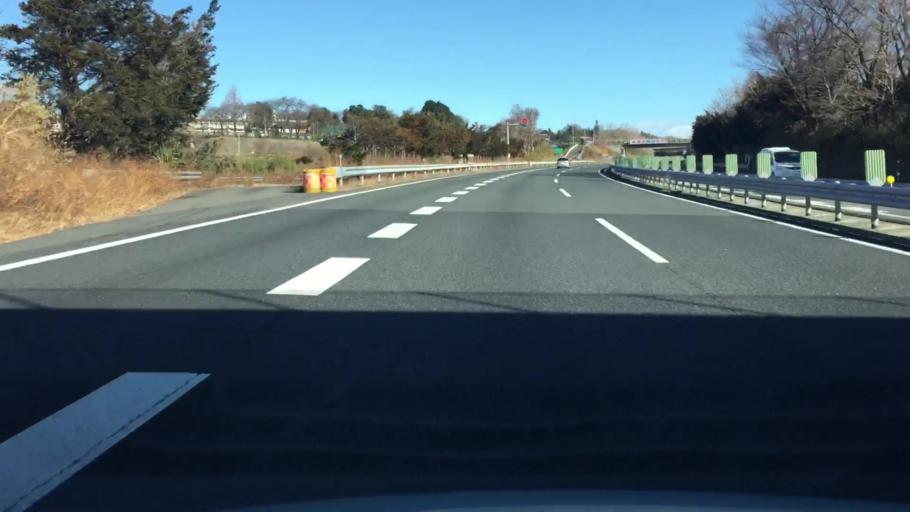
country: JP
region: Gunma
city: Shibukawa
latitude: 36.5139
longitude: 139.0329
